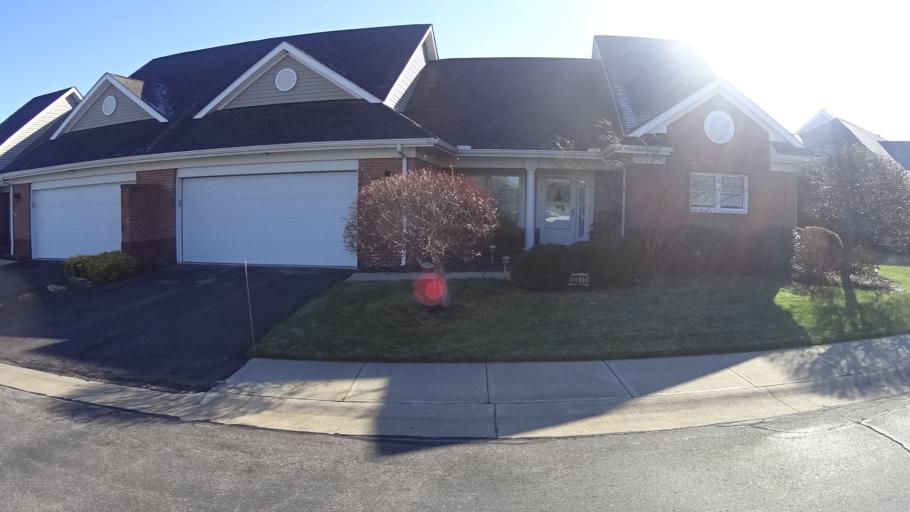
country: US
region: Ohio
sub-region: Lorain County
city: Sheffield
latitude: 41.4230
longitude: -82.0726
